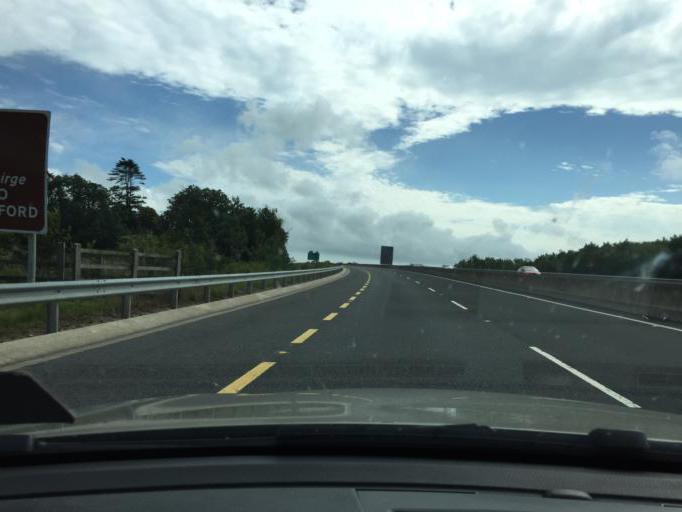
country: IE
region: Leinster
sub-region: Kilkenny
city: Mooncoin
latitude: 52.2541
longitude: -7.1897
